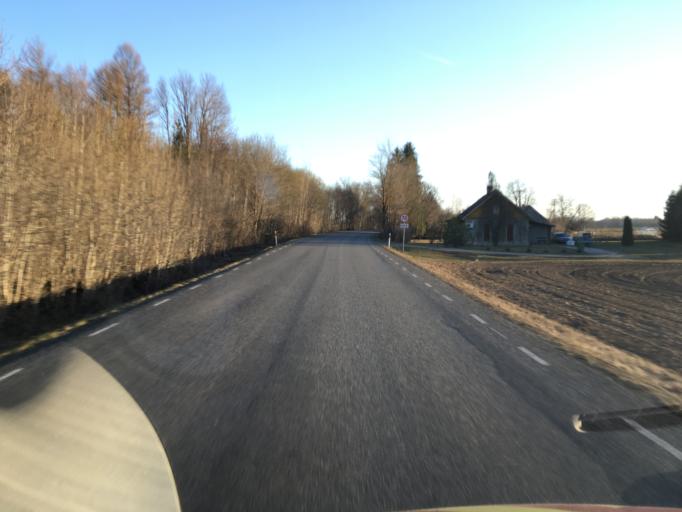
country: EE
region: Raplamaa
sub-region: Kehtna vald
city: Kehtna
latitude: 59.0445
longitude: 24.9441
